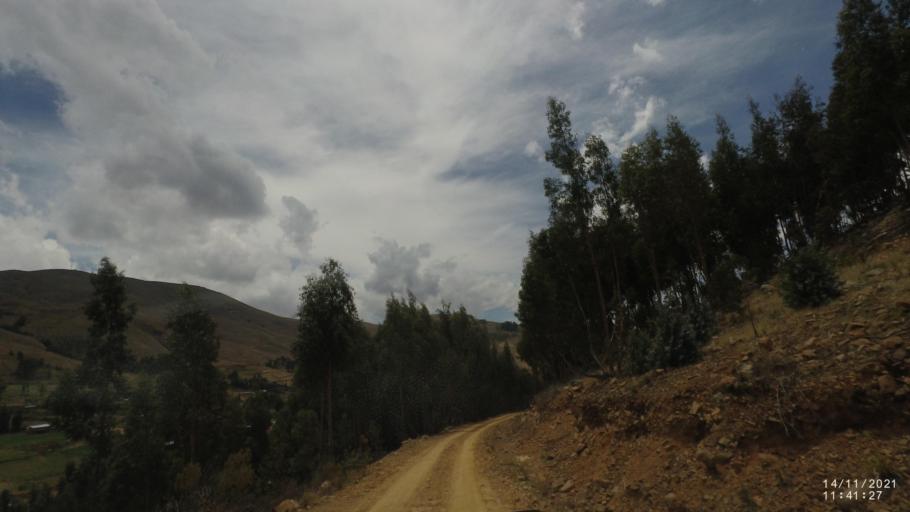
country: BO
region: Cochabamba
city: Colomi
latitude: -17.3531
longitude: -65.9928
